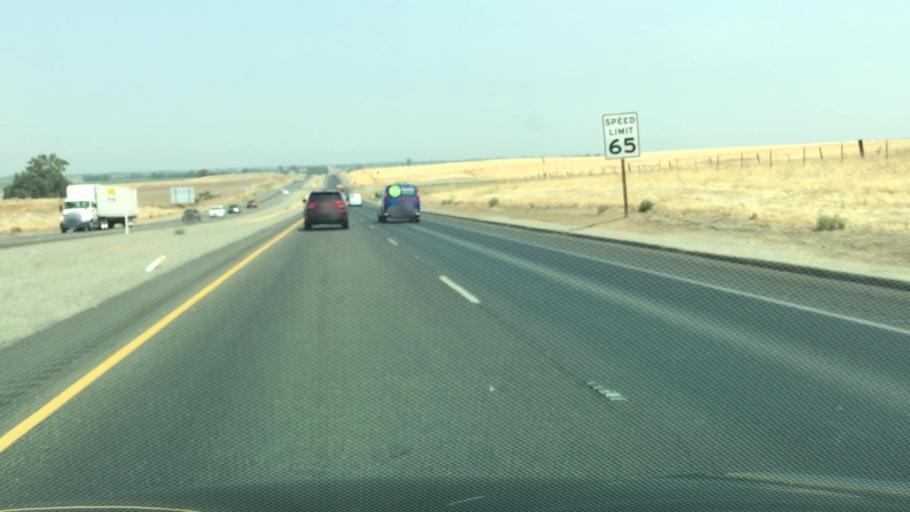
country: US
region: California
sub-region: Merced County
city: Los Banos
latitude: 37.0566
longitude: -120.9589
